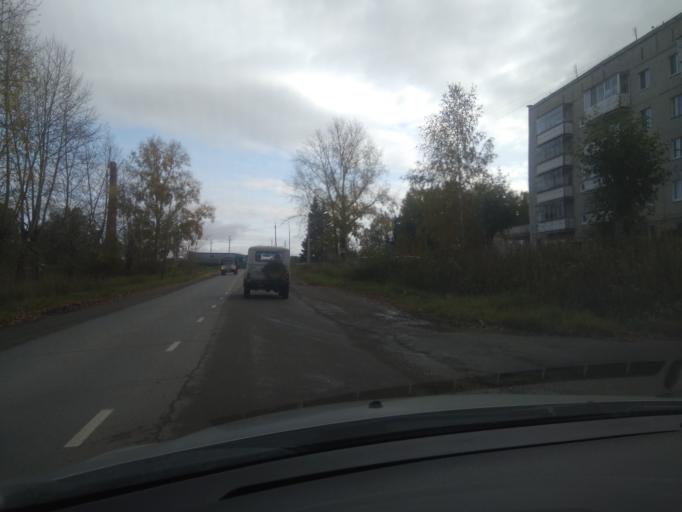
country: RU
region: Sverdlovsk
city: Nikolo-Pavlovskoye
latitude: 57.8006
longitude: 60.0515
